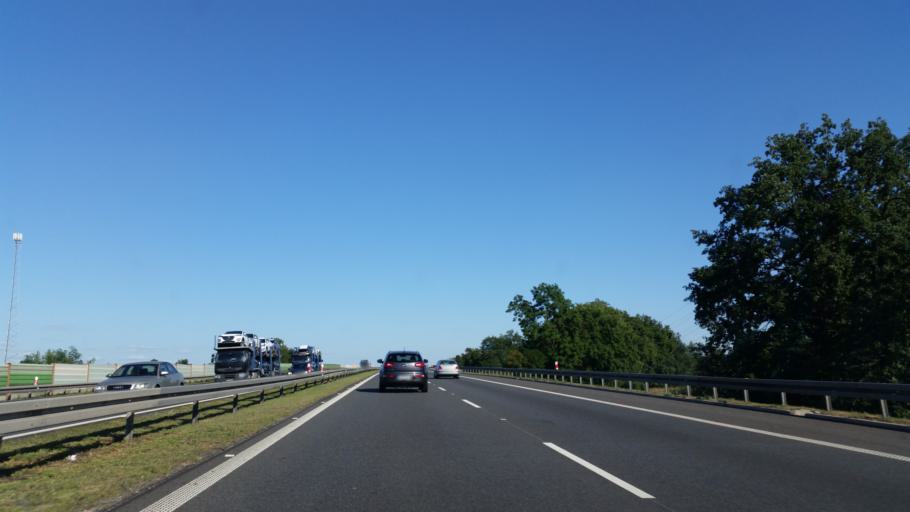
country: PL
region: Lower Silesian Voivodeship
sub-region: Powiat strzelinski
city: Wiazow
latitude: 50.8380
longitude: 17.2737
